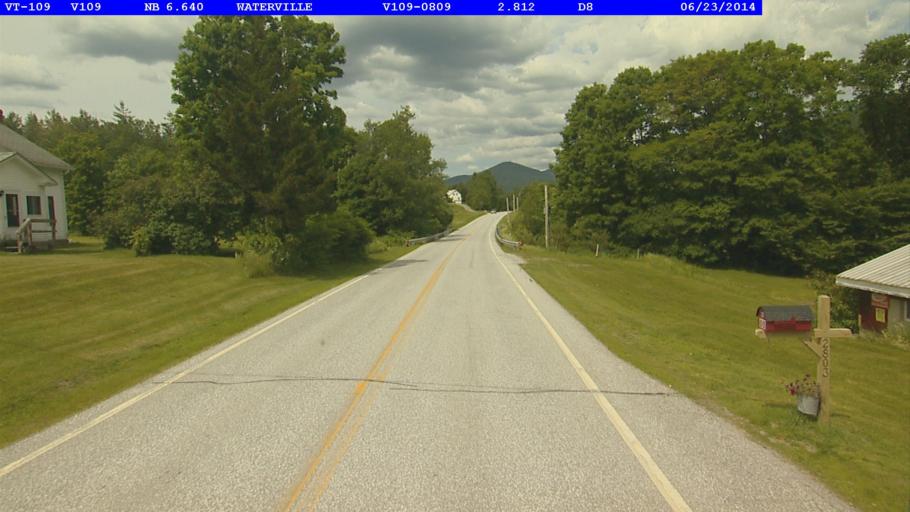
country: US
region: Vermont
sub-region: Lamoille County
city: Johnson
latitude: 44.7184
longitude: -72.7517
